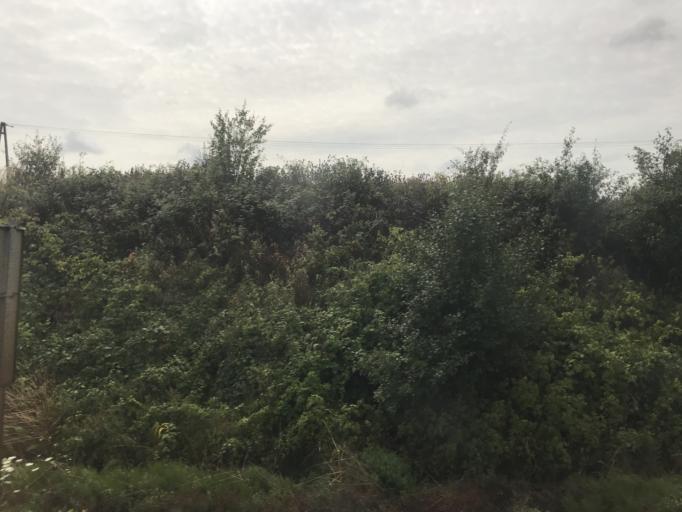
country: PL
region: Kujawsko-Pomorskie
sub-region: Powiat inowroclawski
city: Janikowo
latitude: 52.7278
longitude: 18.0704
